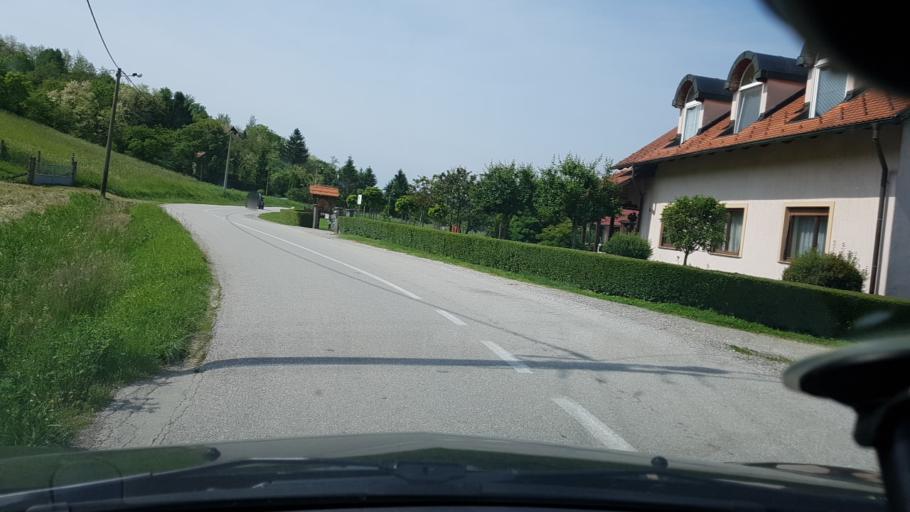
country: HR
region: Krapinsko-Zagorska
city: Marija Bistrica
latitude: 45.9335
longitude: 16.1976
